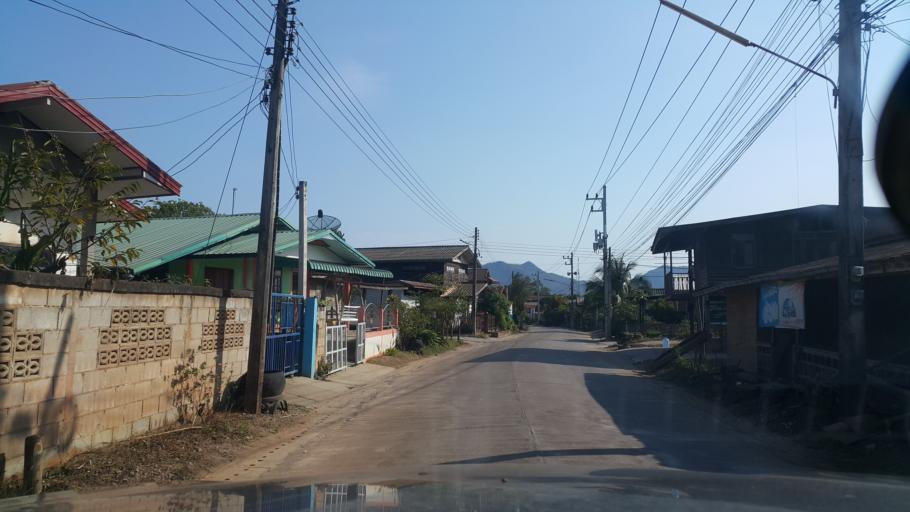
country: TH
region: Loei
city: Chiang Khan
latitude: 17.8527
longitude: 101.6565
